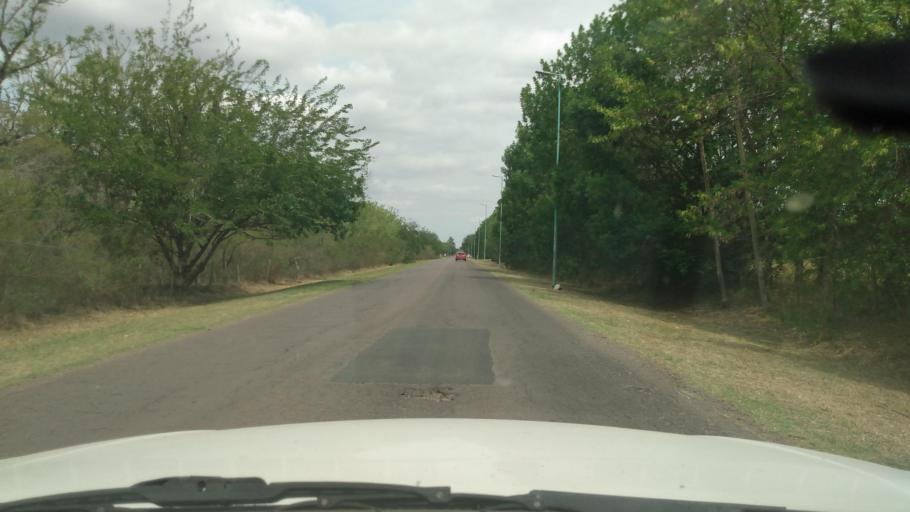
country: AR
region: Buenos Aires
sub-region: Partido de Lujan
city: Lujan
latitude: -34.5578
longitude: -59.1917
